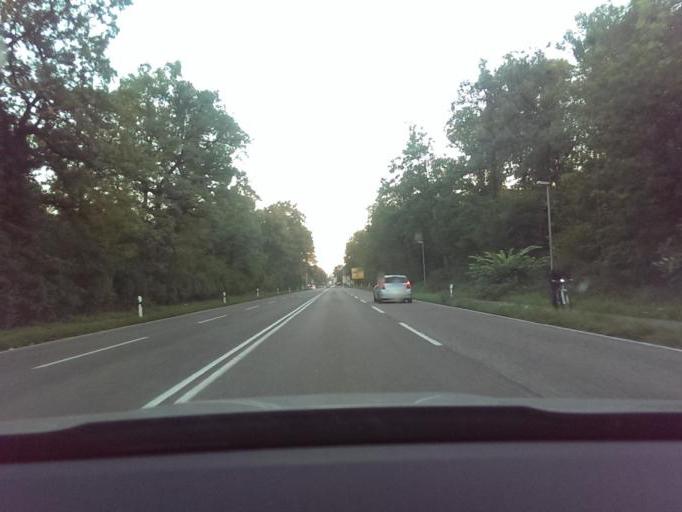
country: DE
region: Baden-Wuerttemberg
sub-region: Karlsruhe Region
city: Karlsruhe
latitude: 49.0275
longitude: 8.3959
